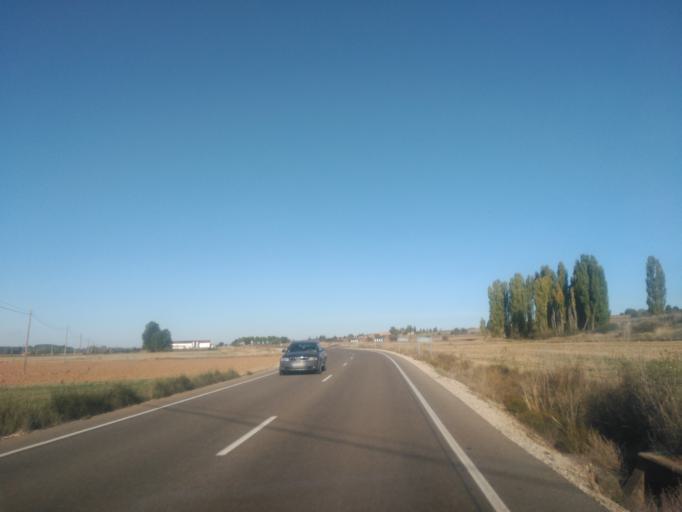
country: ES
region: Castille and Leon
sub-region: Provincia de Burgos
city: San Juan del Monte
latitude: 41.6897
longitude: -3.5121
